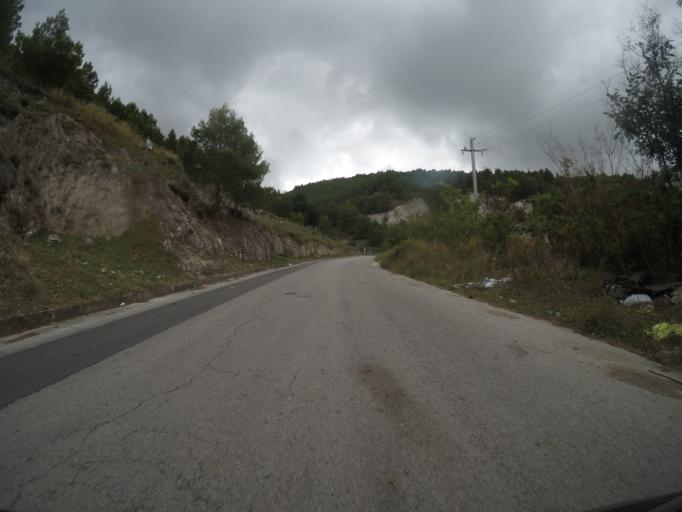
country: IT
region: Sicily
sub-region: Palermo
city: Montelepre
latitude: 38.1159
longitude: 13.1715
